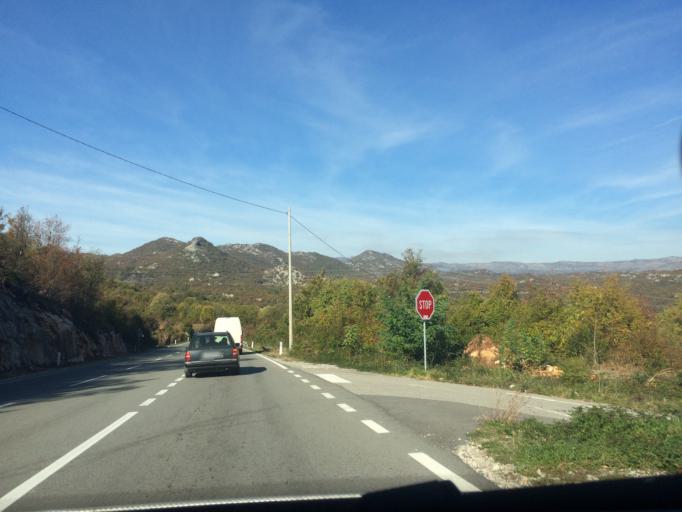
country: ME
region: Cetinje
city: Cetinje
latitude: 42.3815
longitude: 19.0580
